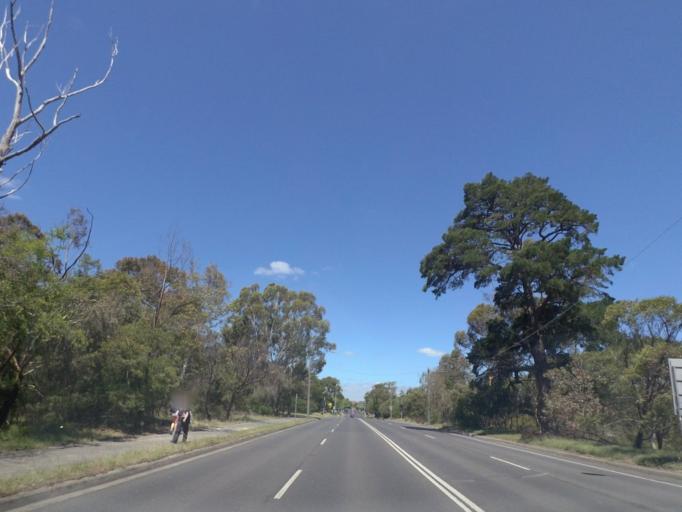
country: AU
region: Victoria
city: Abbotsford
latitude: -37.8041
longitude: 145.0126
